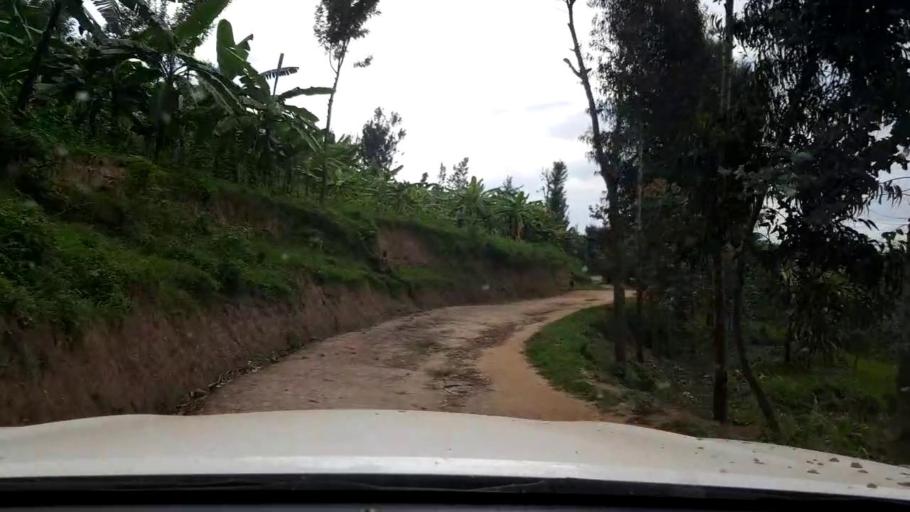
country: RW
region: Western Province
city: Kibuye
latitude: -2.0008
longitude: 29.3714
